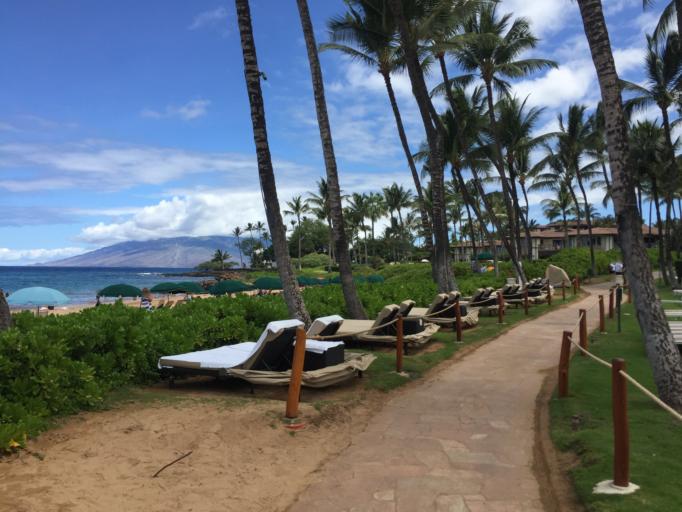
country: US
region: Hawaii
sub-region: Maui County
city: Kihei
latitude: 20.6838
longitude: -156.4429
